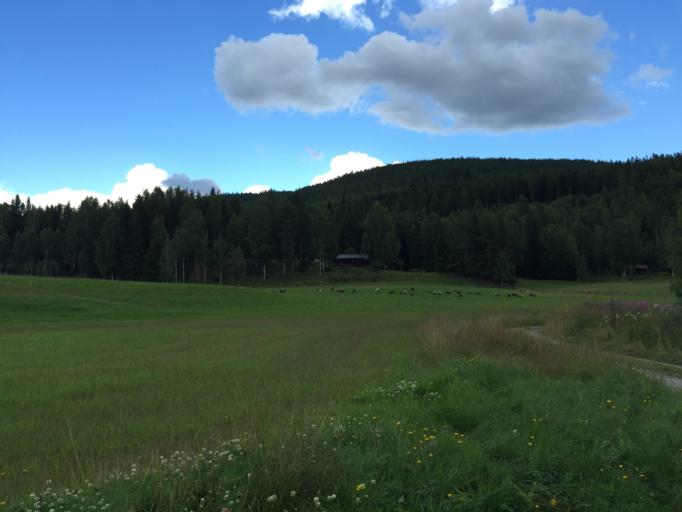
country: SE
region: Gaevleborg
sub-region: Ljusdals Kommun
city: Jaervsoe
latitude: 61.7440
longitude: 16.2753
